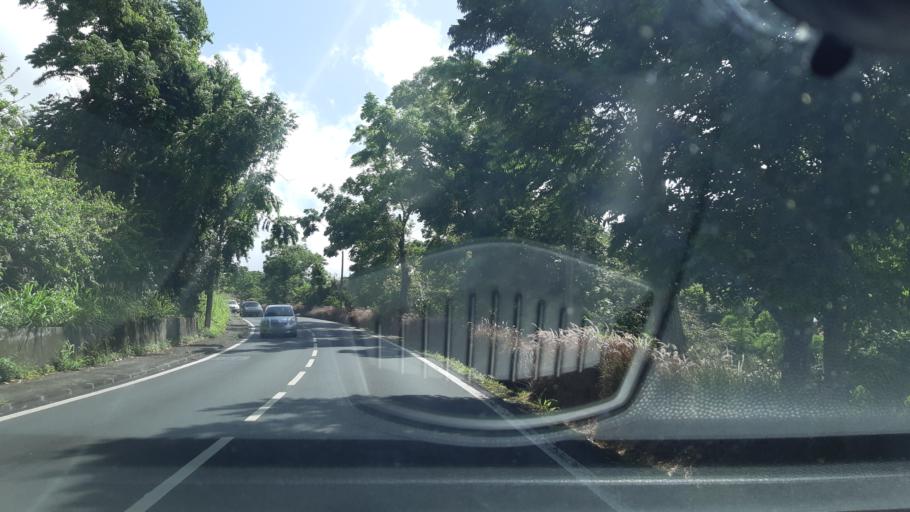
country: GP
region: Guadeloupe
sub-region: Guadeloupe
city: Saint-Claude
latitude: 16.0142
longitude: -61.7092
